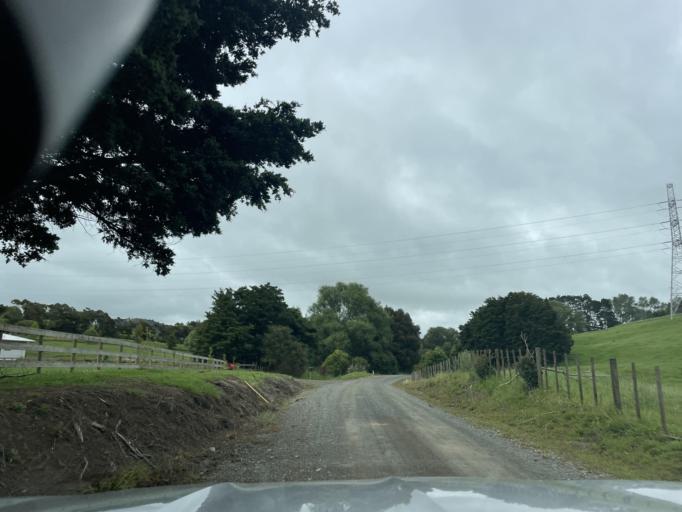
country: NZ
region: Northland
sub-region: Whangarei
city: Ruakaka
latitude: -36.0978
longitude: 174.4160
